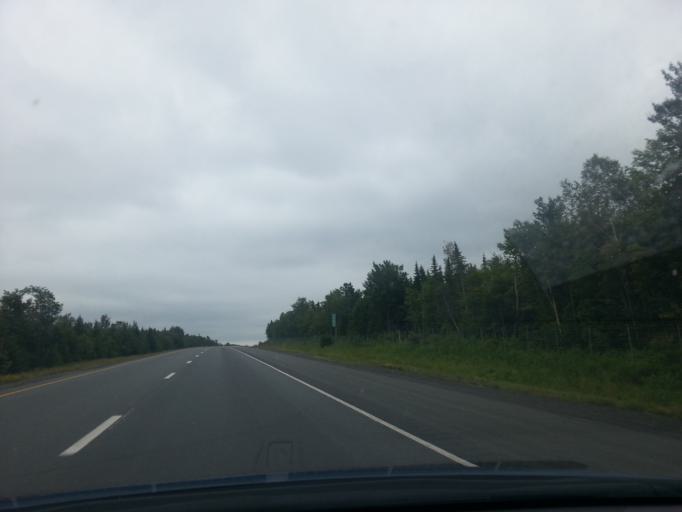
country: US
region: Maine
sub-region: Aroostook County
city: Houlton
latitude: 46.0189
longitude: -67.5531
